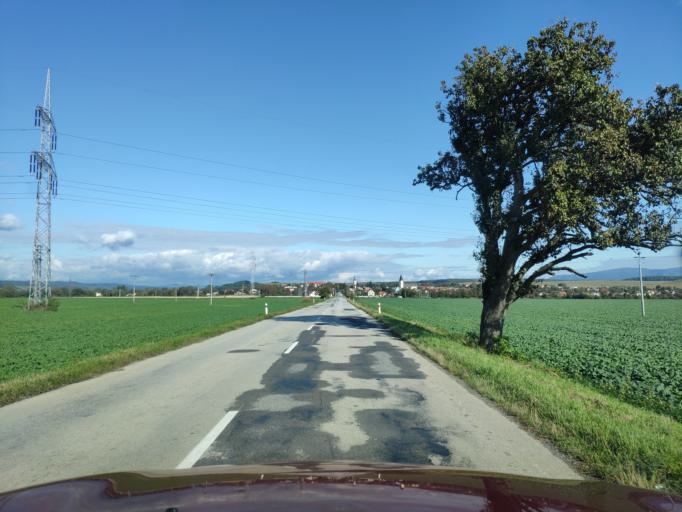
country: SK
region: Presovsky
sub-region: Okres Presov
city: Presov
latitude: 48.8622
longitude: 21.2708
